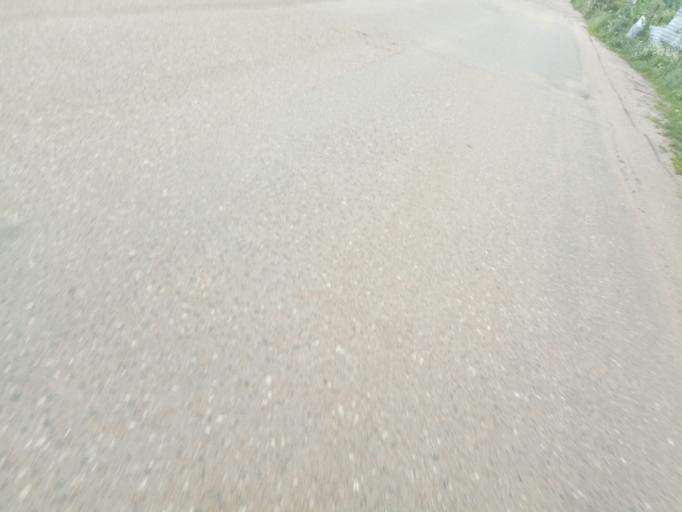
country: RU
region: Jaroslavl
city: Yaroslavl
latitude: 57.6558
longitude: 39.9802
